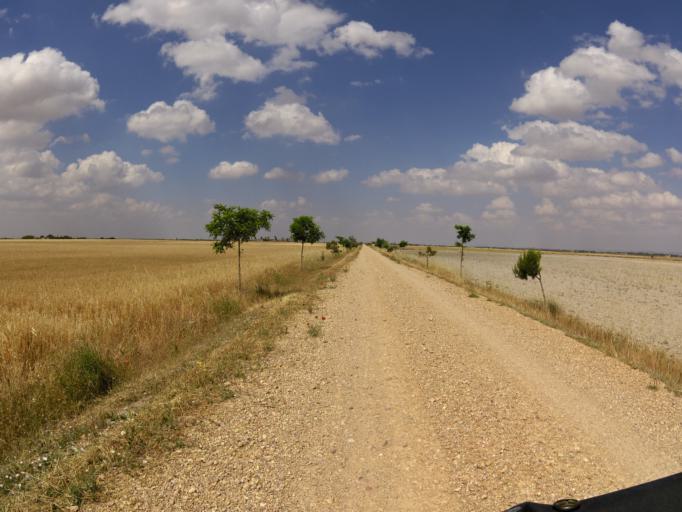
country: ES
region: Castille-La Mancha
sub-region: Provincia de Albacete
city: Albacete
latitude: 38.9355
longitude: -1.9879
